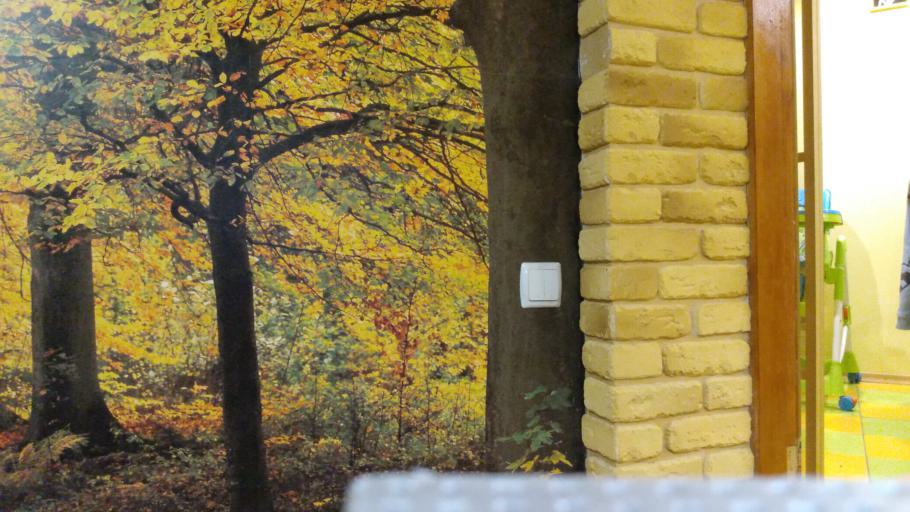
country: RU
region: Vologda
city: Ustyuzhna
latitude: 59.1180
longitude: 36.1904
